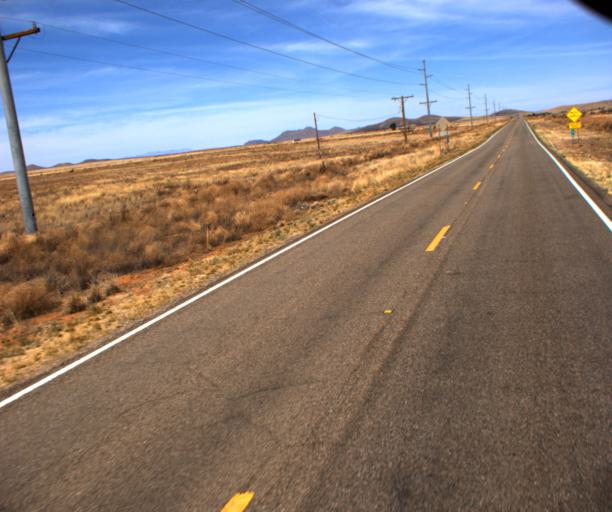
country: US
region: Arizona
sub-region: Cochise County
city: Tombstone
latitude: 31.8519
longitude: -109.6951
